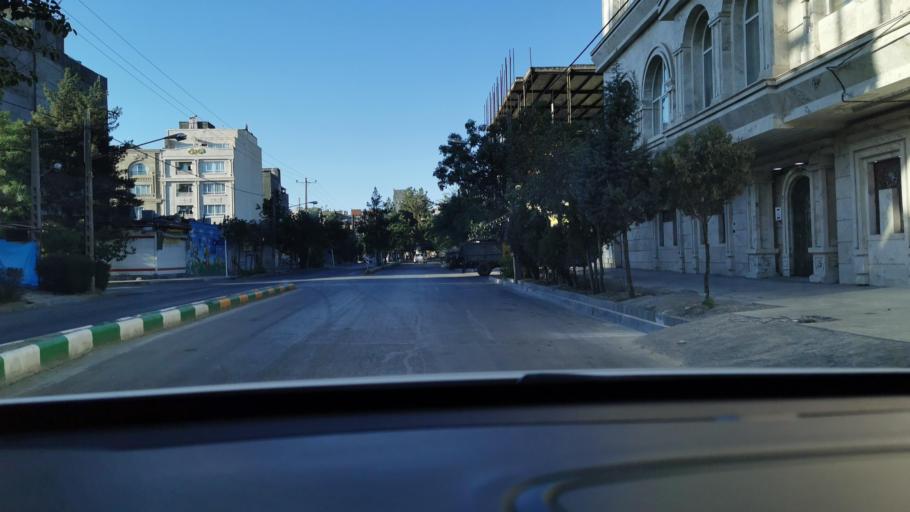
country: IR
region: Razavi Khorasan
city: Mashhad
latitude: 36.3614
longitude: 59.4903
